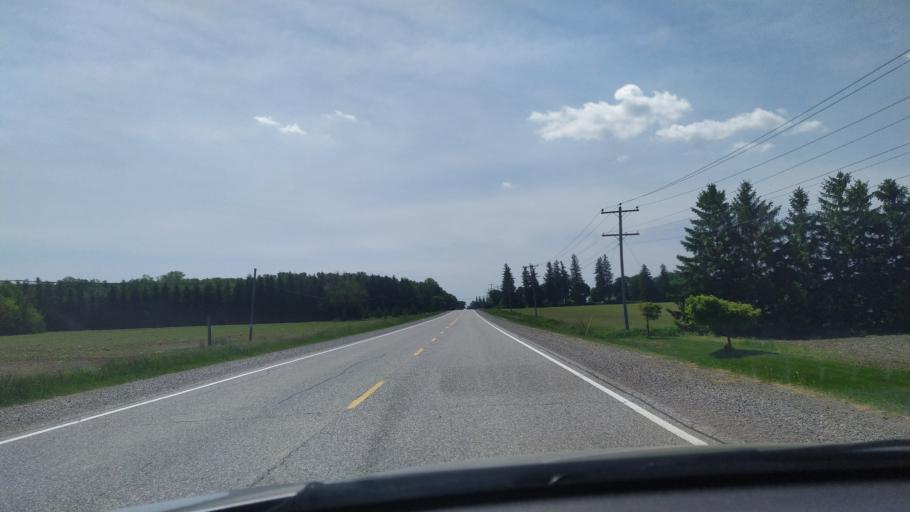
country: CA
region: Ontario
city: Dorchester
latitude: 43.1028
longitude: -81.0117
